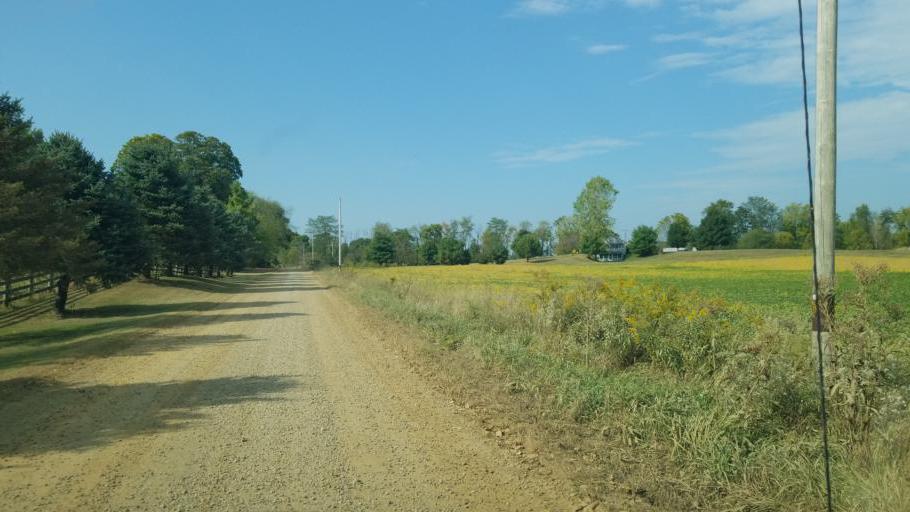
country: US
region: Ohio
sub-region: Knox County
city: Mount Vernon
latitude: 40.3312
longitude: -82.4942
